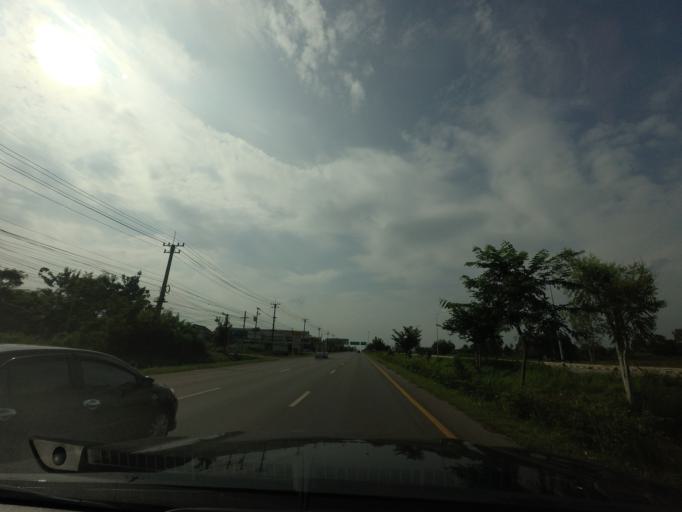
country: TH
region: Nong Khai
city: Nong Khai
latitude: 17.8167
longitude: 102.7584
